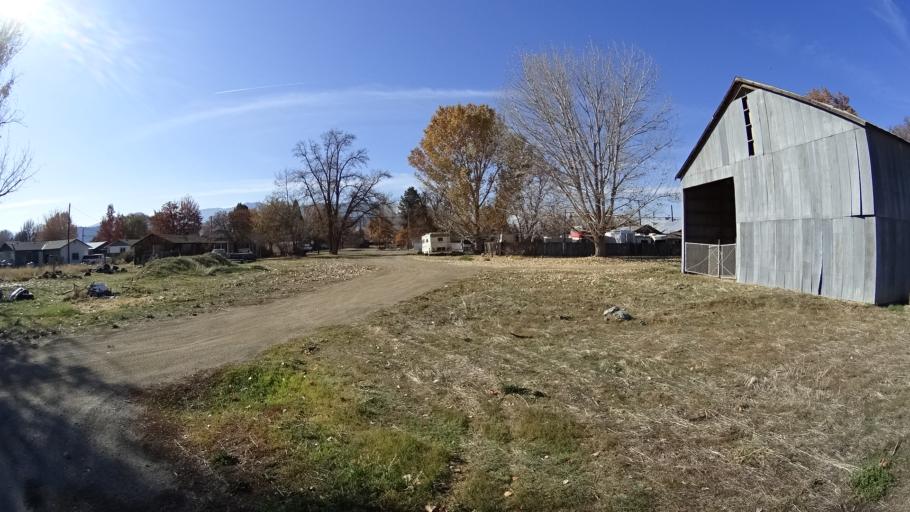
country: US
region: California
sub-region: Siskiyou County
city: Montague
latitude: 41.6443
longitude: -122.5213
